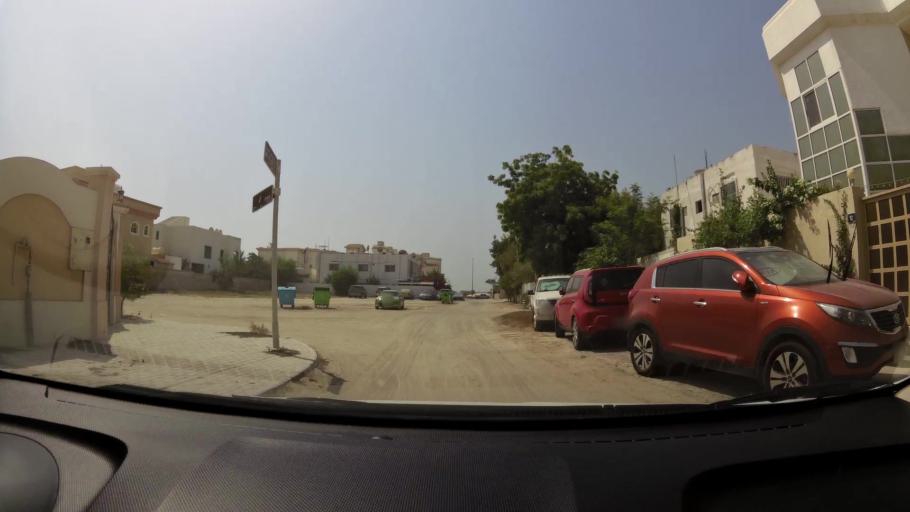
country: AE
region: Ajman
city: Ajman
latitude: 25.3919
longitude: 55.4213
